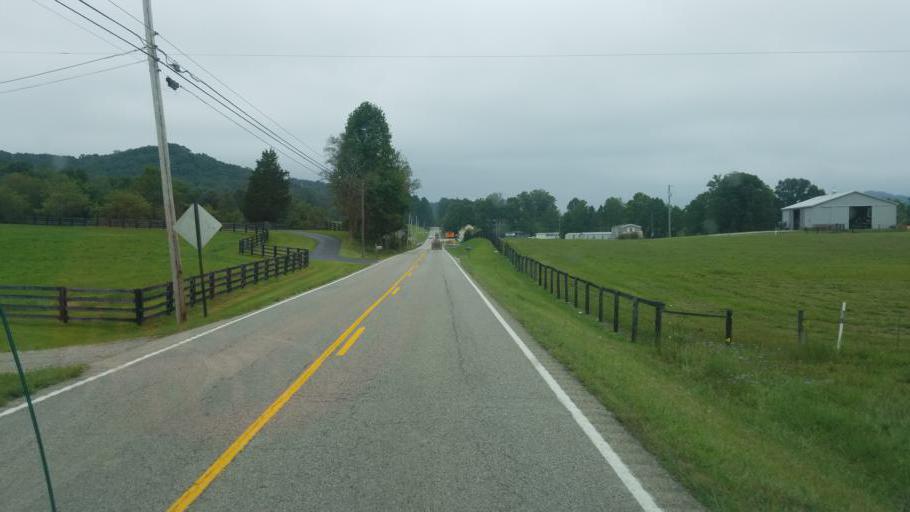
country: US
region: Kentucky
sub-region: Rowan County
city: Morehead
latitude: 38.2195
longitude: -83.4708
